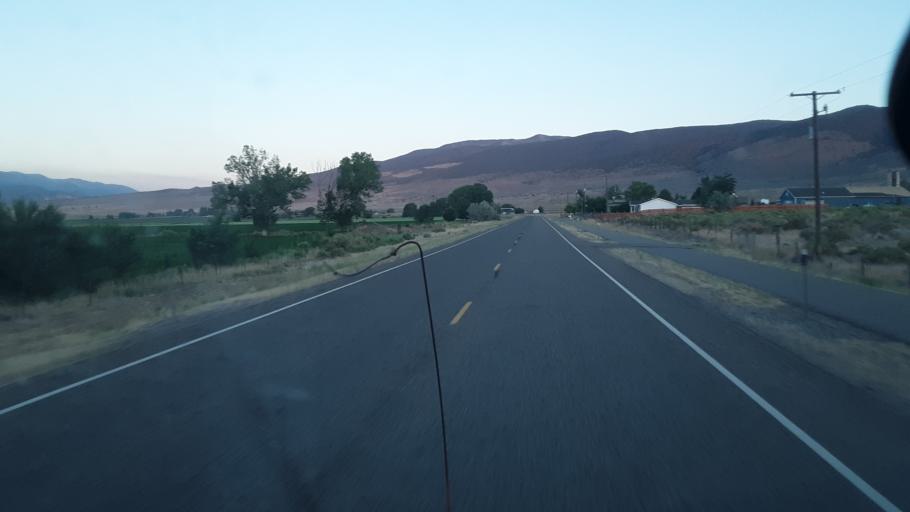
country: US
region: Utah
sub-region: Sevier County
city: Monroe
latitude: 38.6541
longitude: -112.1951
